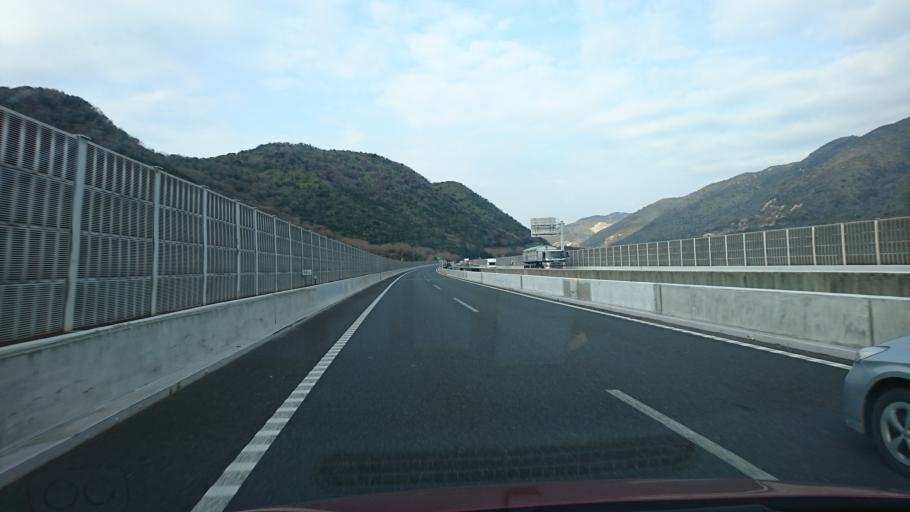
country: JP
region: Hyogo
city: Kariya
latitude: 34.7734
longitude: 134.3687
